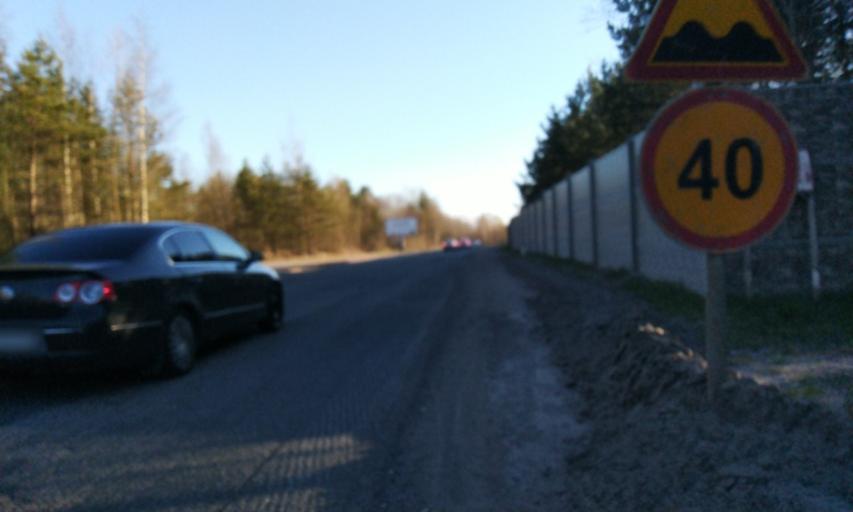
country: RU
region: Leningrad
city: Toksovo
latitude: 60.1254
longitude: 30.5150
